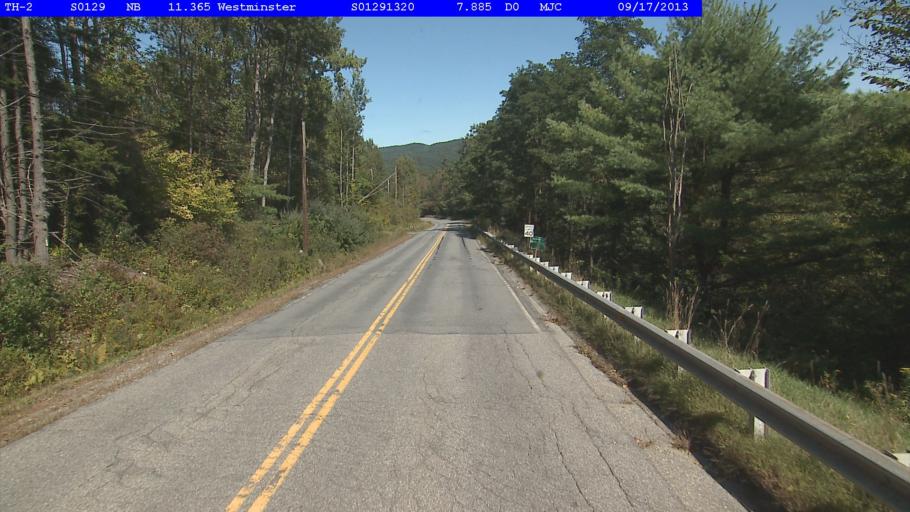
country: US
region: Vermont
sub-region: Windham County
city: Rockingham
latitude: 43.1260
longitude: -72.5267
